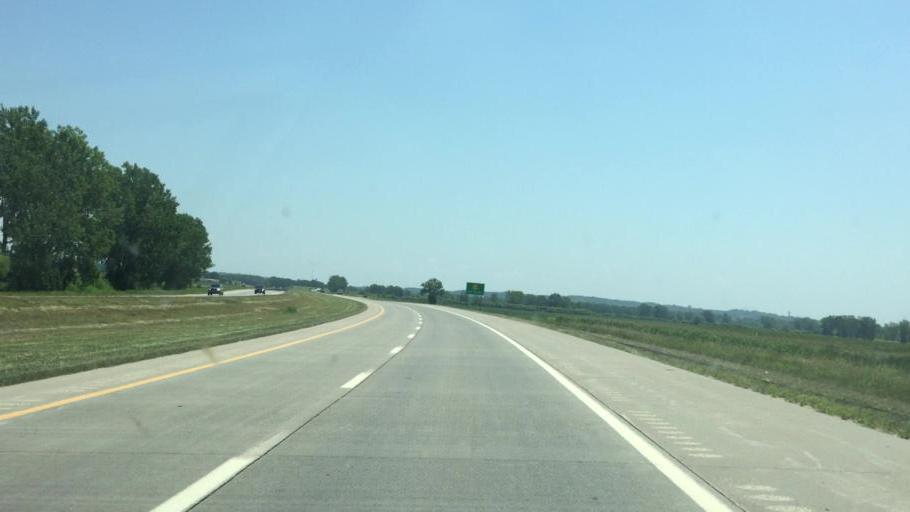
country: US
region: Kansas
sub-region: Doniphan County
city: Wathena
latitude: 39.7404
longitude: -94.9146
